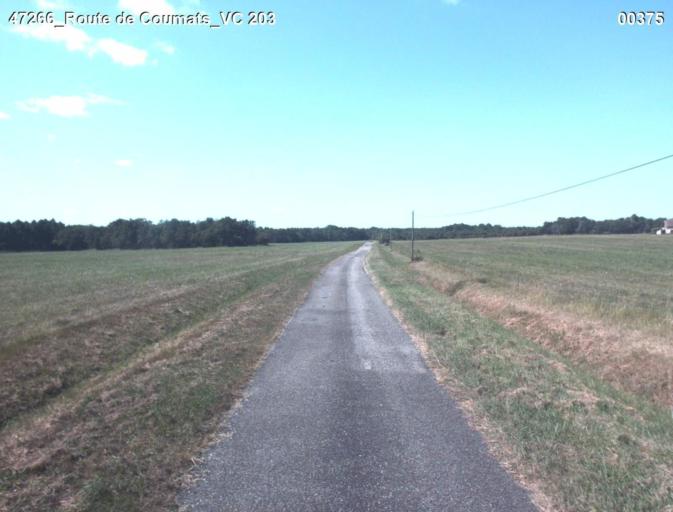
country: FR
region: Aquitaine
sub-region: Departement des Landes
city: Gabarret
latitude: 44.0143
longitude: 0.0897
